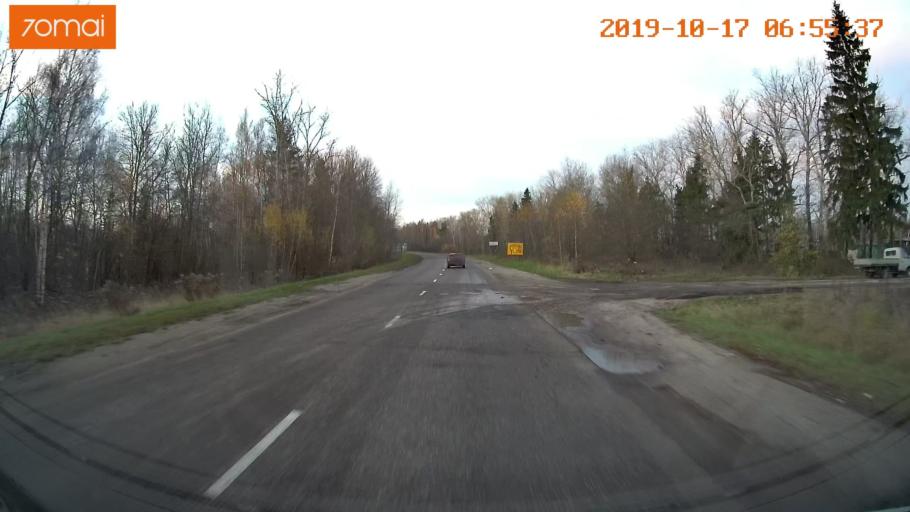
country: RU
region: Vladimir
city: Suzdal'
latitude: 56.4547
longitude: 40.4552
